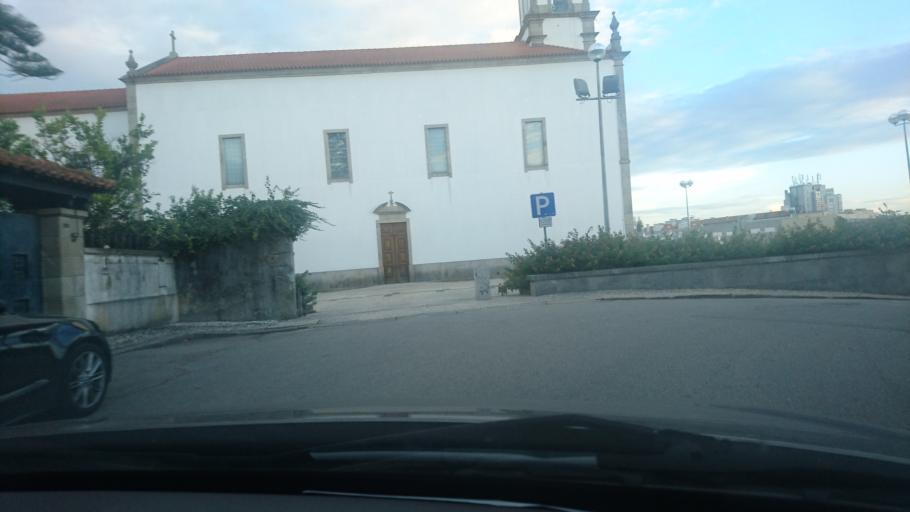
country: PT
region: Aveiro
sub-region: Sao Joao da Madeira
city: Sao Joao da Madeira
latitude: 40.8957
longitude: -8.4915
